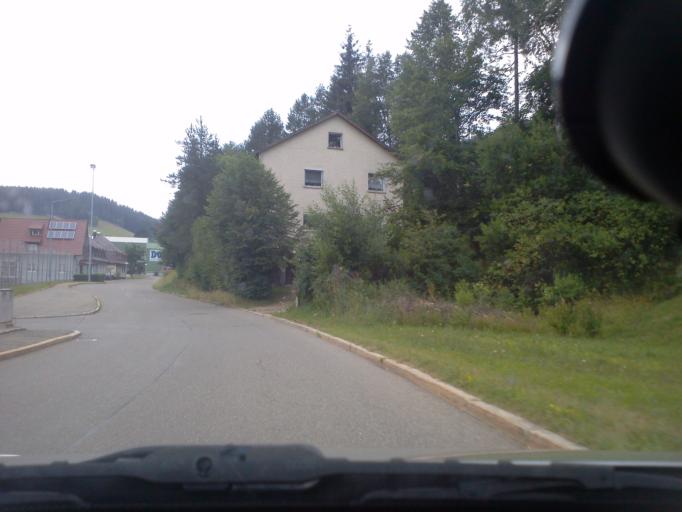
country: DE
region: Baden-Wuerttemberg
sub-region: Freiburg Region
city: Vohrenbach
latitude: 48.0491
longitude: 8.3053
